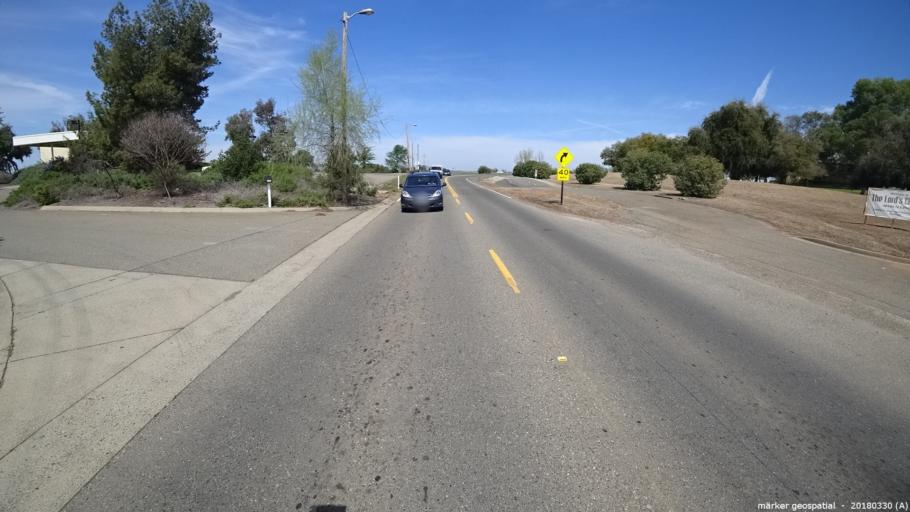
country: US
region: California
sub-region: Sacramento County
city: Rancho Cordova
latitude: 38.5498
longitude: -121.2809
